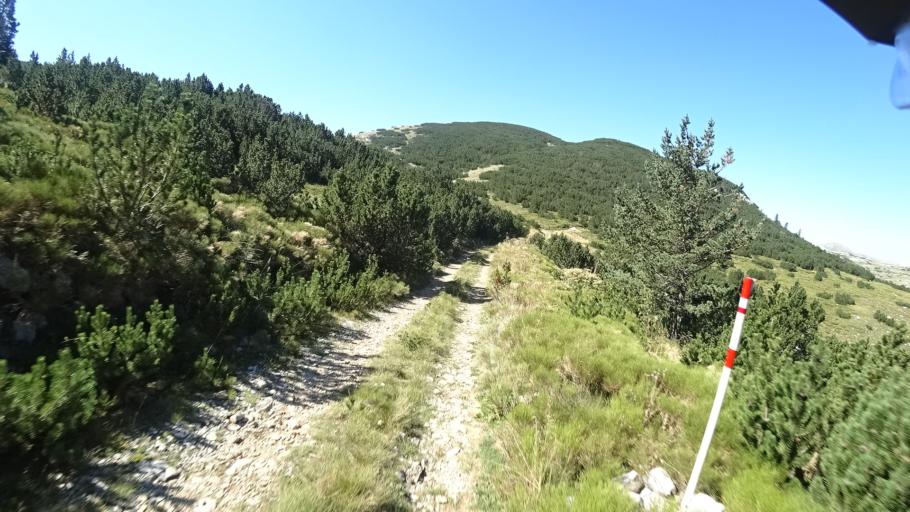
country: HR
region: Splitsko-Dalmatinska
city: Hrvace
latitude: 43.9397
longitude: 16.5789
